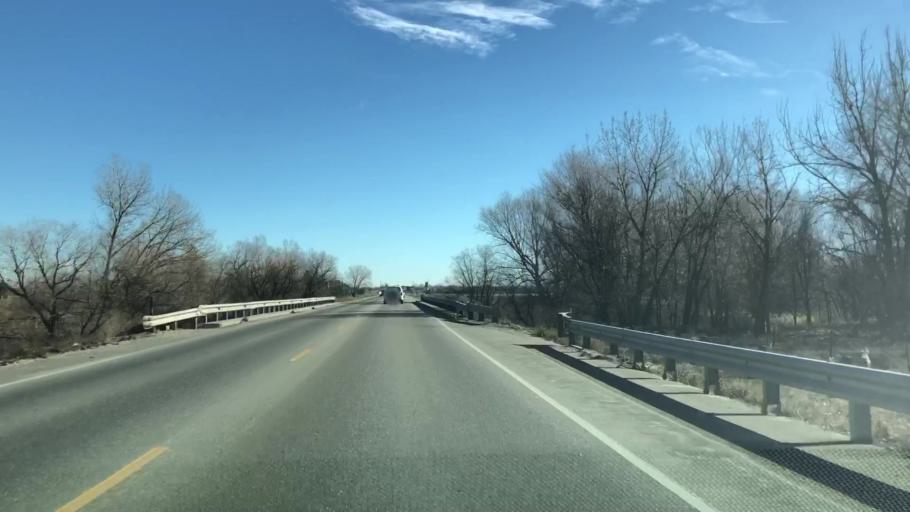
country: US
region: Colorado
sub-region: Weld County
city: Windsor
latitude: 40.4793
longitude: -104.9540
